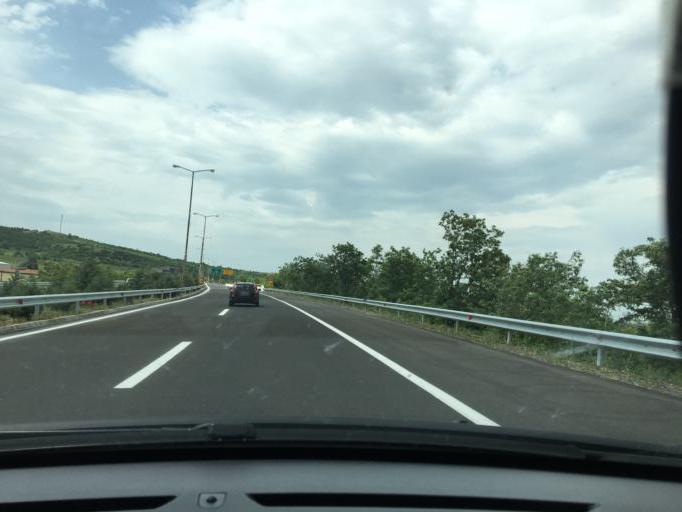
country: MK
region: Demir Kapija
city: Demir Kapija
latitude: 41.4158
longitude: 22.2386
